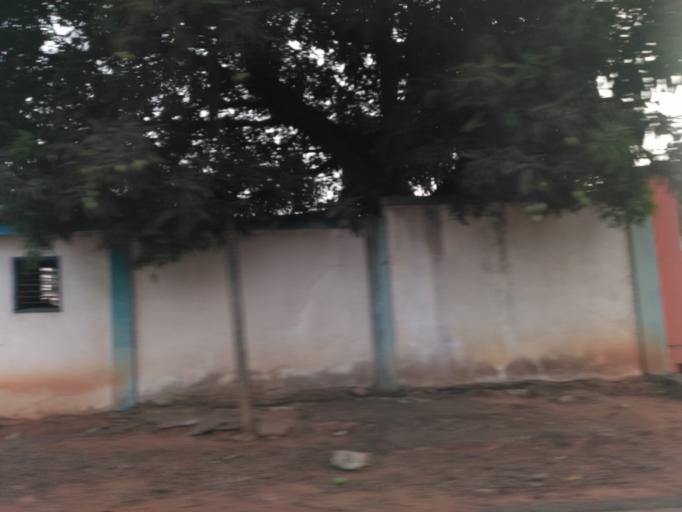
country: GH
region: Ashanti
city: Kumasi
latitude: 6.6796
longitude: -1.6120
